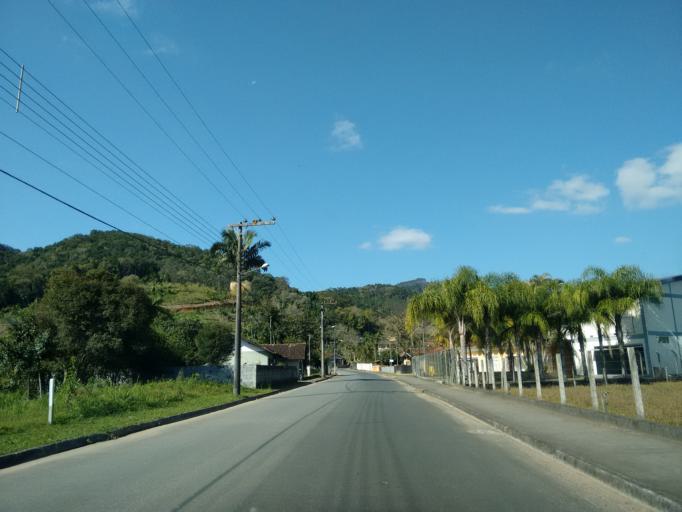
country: BR
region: Santa Catarina
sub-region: Pomerode
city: Pomerode
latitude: -26.7388
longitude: -49.1653
